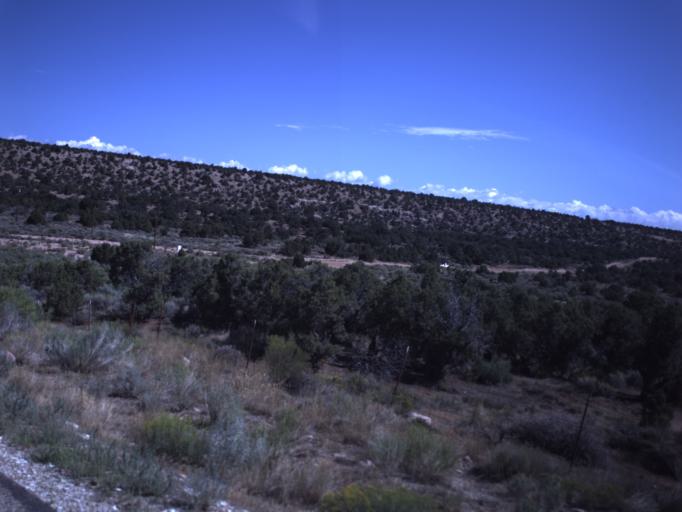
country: US
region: Utah
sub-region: Duchesne County
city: Duchesne
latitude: 40.3064
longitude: -110.3732
